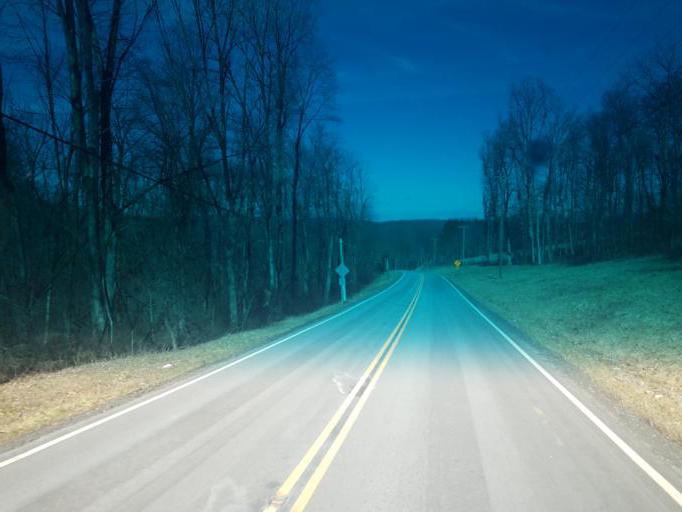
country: US
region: Ohio
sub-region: Knox County
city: Danville
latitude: 40.5009
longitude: -82.2223
